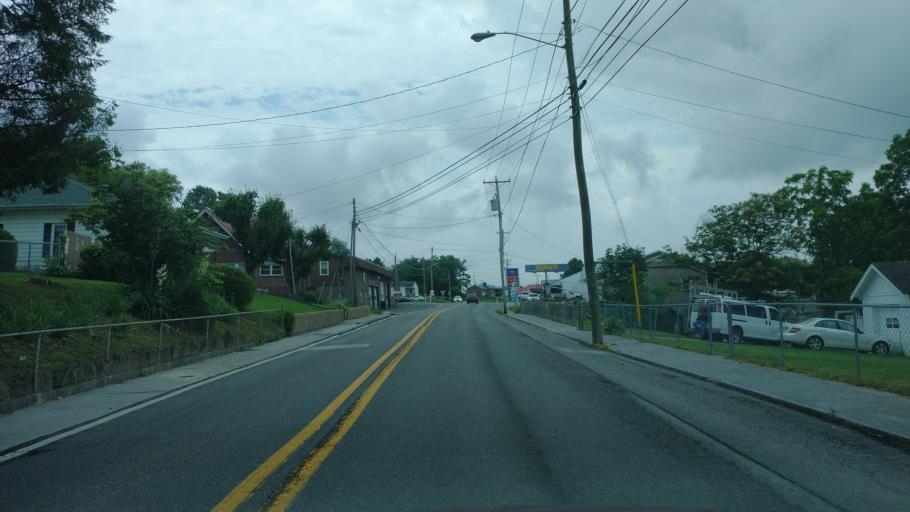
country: US
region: West Virginia
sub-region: Mercer County
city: Athens
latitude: 37.4176
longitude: -81.0157
